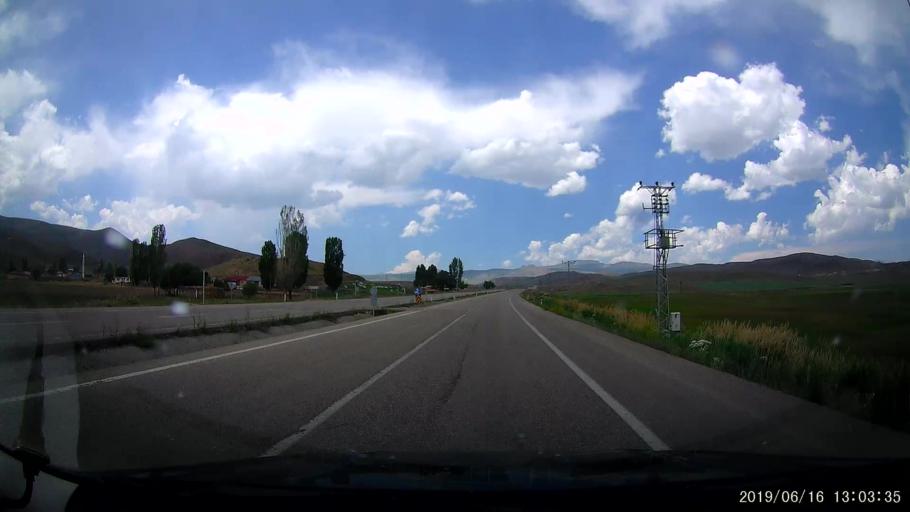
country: TR
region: Agri
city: Sulucem
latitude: 39.5829
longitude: 43.7875
